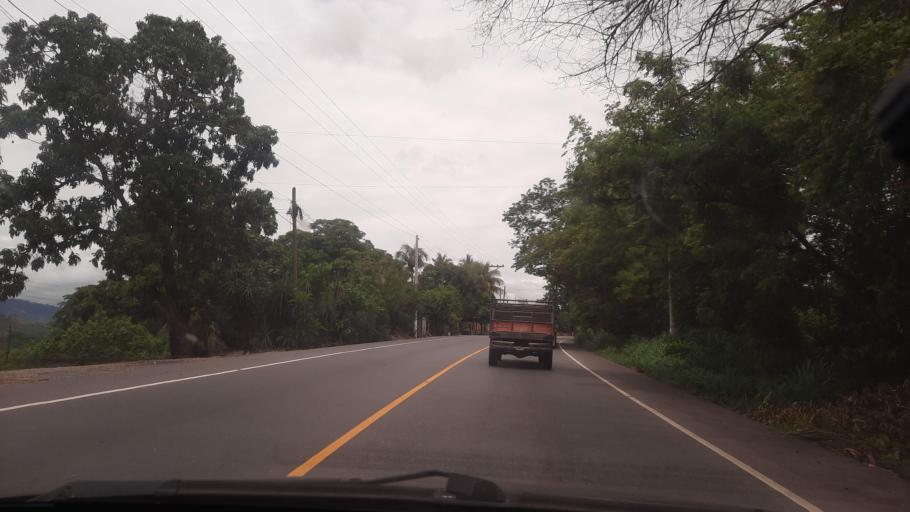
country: GT
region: Zacapa
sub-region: Municipio de Zacapa
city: Gualan
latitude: 15.1447
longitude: -89.3281
